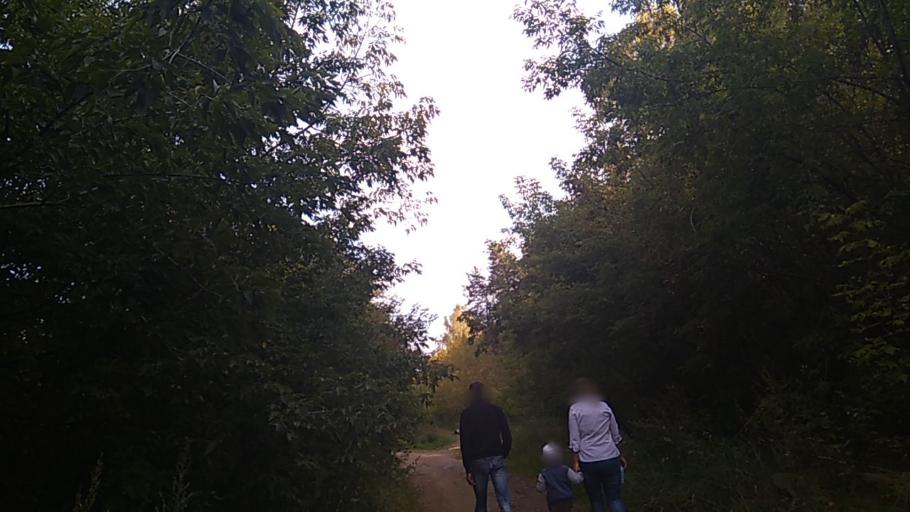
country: RU
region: Sverdlovsk
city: Pokrovskoye
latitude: 56.4344
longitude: 61.5935
